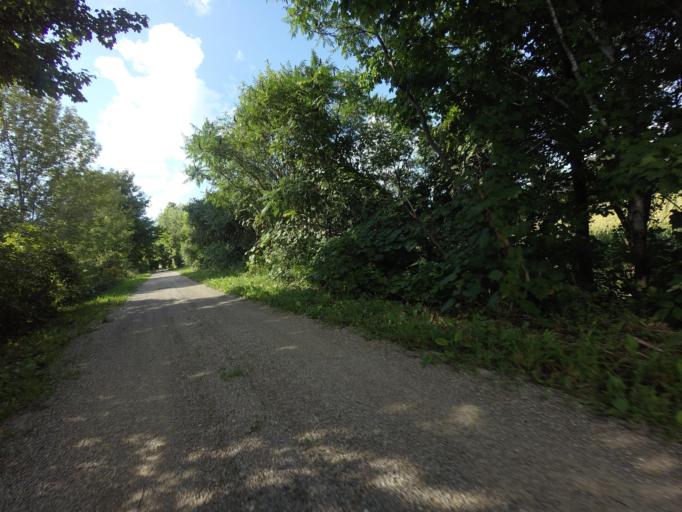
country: CA
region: Ontario
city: Goderich
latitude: 43.7489
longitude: -81.5001
